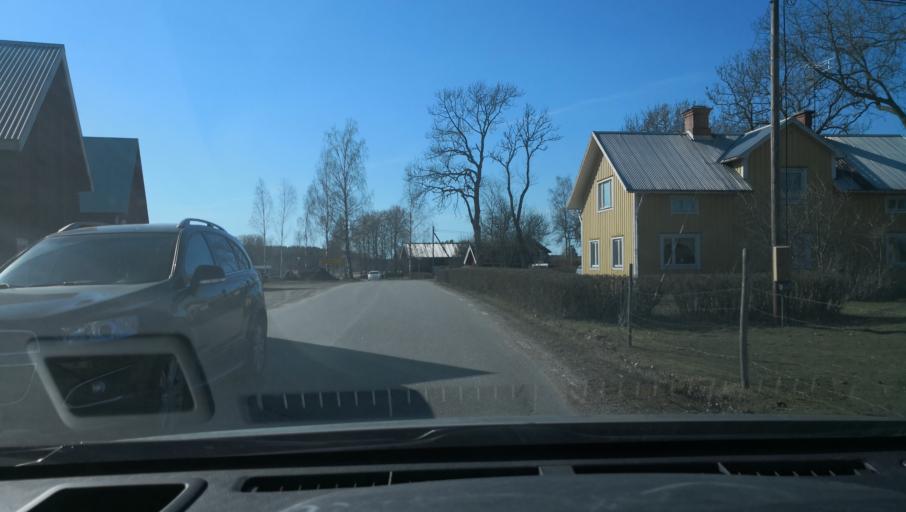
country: SE
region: Vaestmanland
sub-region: Sala Kommun
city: Sala
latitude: 60.0854
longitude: 16.5243
